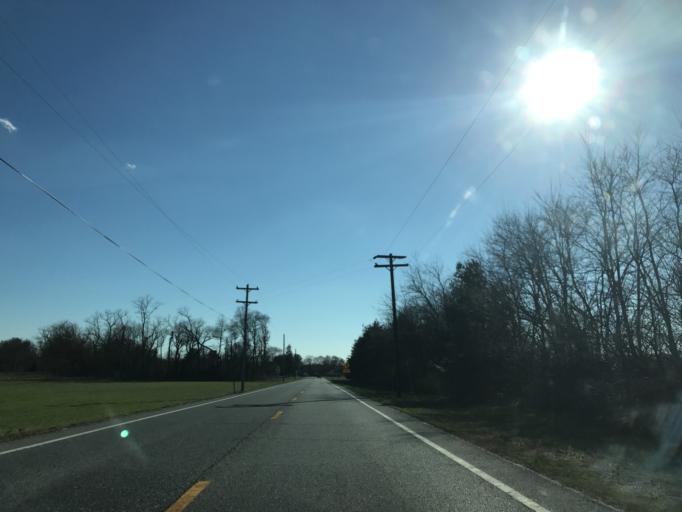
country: US
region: Maryland
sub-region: Caroline County
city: Ridgely
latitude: 39.0376
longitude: -75.8720
